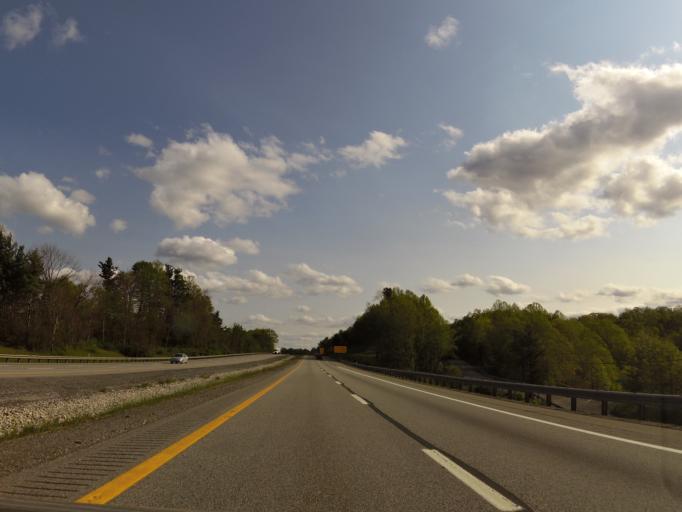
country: US
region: West Virginia
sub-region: Raleigh County
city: Shady Spring
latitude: 37.5483
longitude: -81.1149
